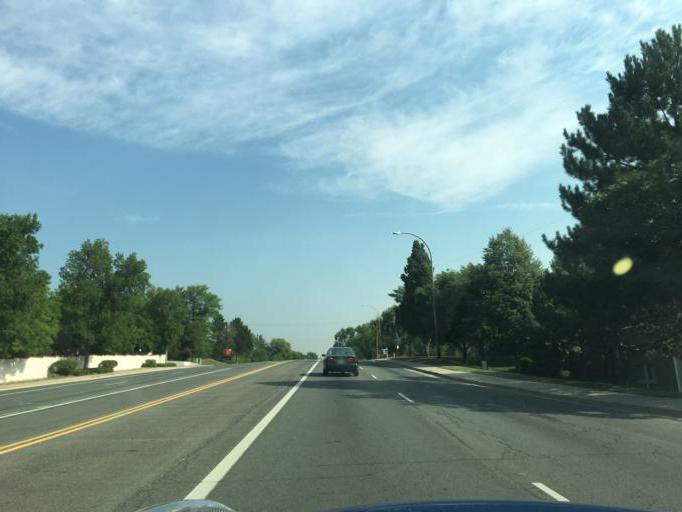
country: US
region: Colorado
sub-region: Jefferson County
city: Edgewater
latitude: 39.7489
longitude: -105.0814
